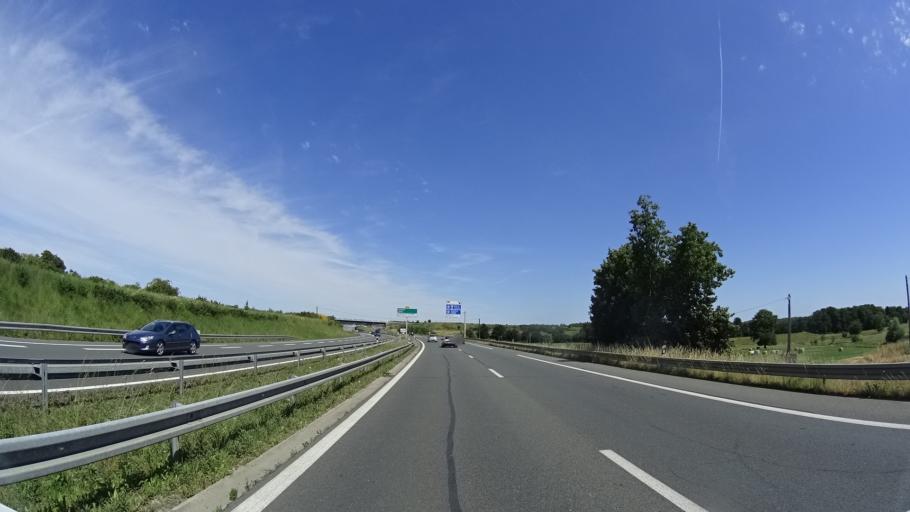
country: FR
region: Pays de la Loire
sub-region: Departement de Maine-et-Loire
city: Beaucouze
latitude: 47.4889
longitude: -0.6222
